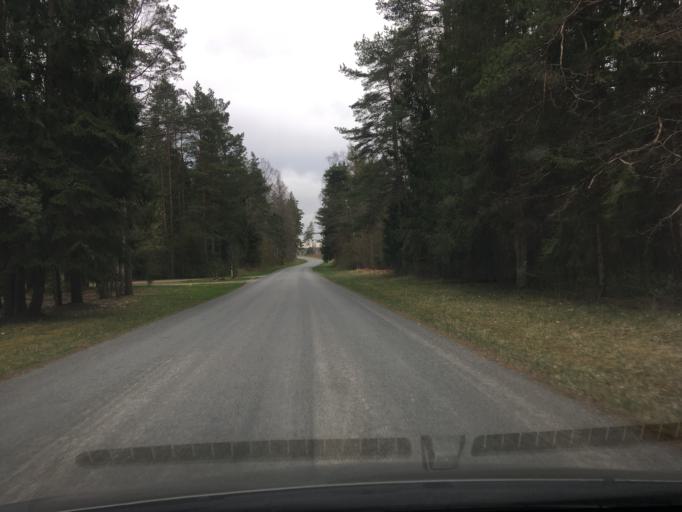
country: EE
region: Harju
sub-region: Raasiku vald
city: Raasiku
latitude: 59.2119
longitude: 25.1833
